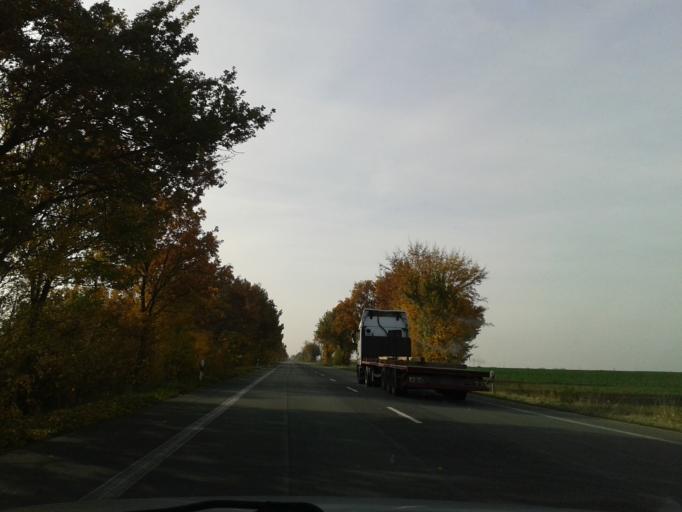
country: DE
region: North Rhine-Westphalia
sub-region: Regierungsbezirk Detmold
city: Buren
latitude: 51.5829
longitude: 8.5641
